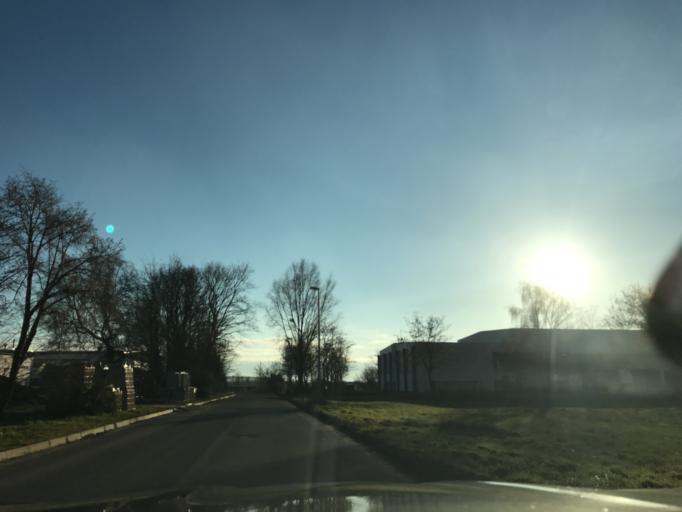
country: DE
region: Saxony-Anhalt
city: Mockern
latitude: 52.1554
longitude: 11.9432
